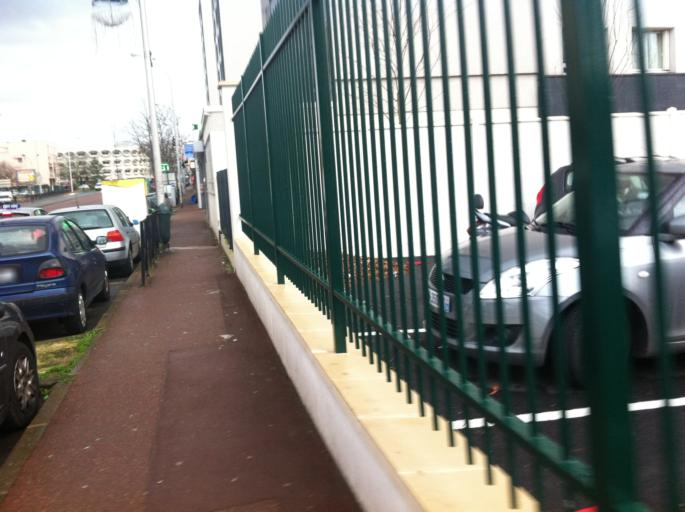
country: FR
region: Ile-de-France
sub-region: Departement du Val-de-Marne
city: Creteil
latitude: 48.8029
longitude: 2.4716
